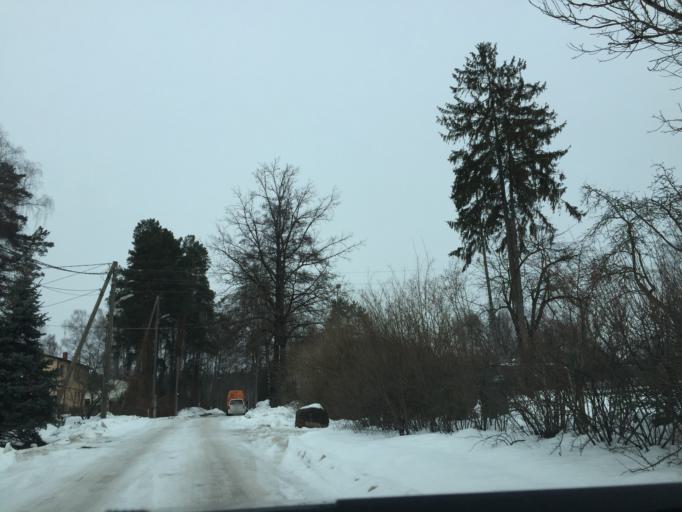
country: LV
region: Ogre
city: Ogre
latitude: 56.8211
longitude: 24.5751
